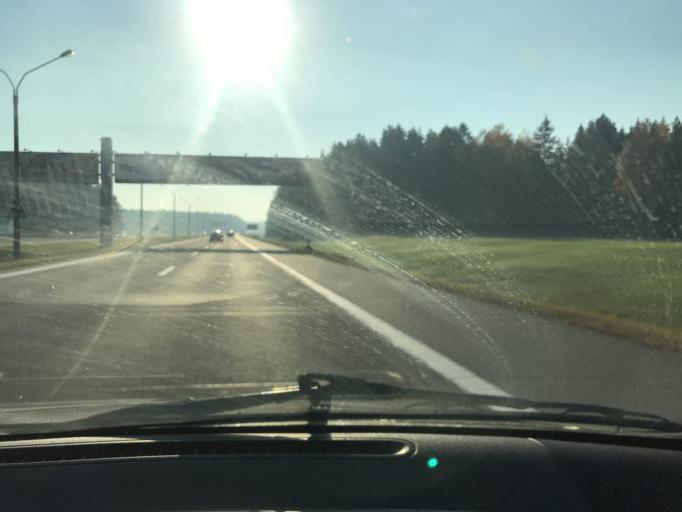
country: BY
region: Minsk
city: Slabada
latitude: 53.9604
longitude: 27.9639
